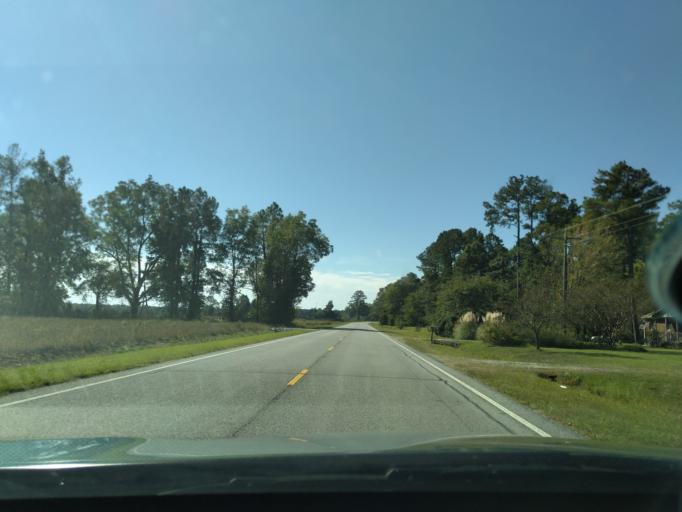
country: US
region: North Carolina
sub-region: Beaufort County
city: Belhaven
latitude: 35.6236
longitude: -76.8104
